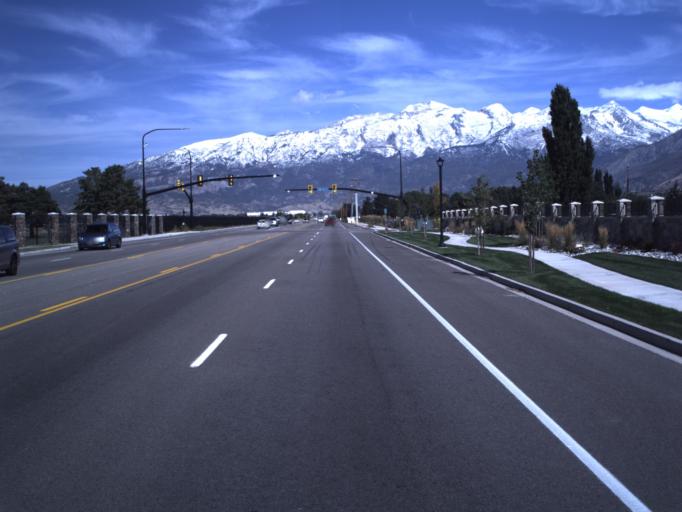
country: US
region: Utah
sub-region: Utah County
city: Cedar Hills
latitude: 40.3980
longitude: -111.7732
